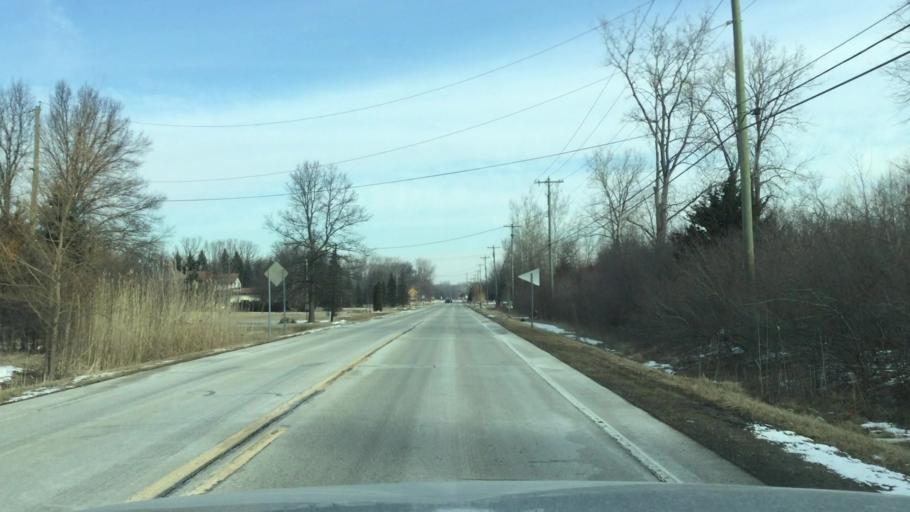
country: US
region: Michigan
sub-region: Wayne County
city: Flat Rock
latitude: 42.1249
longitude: -83.2897
